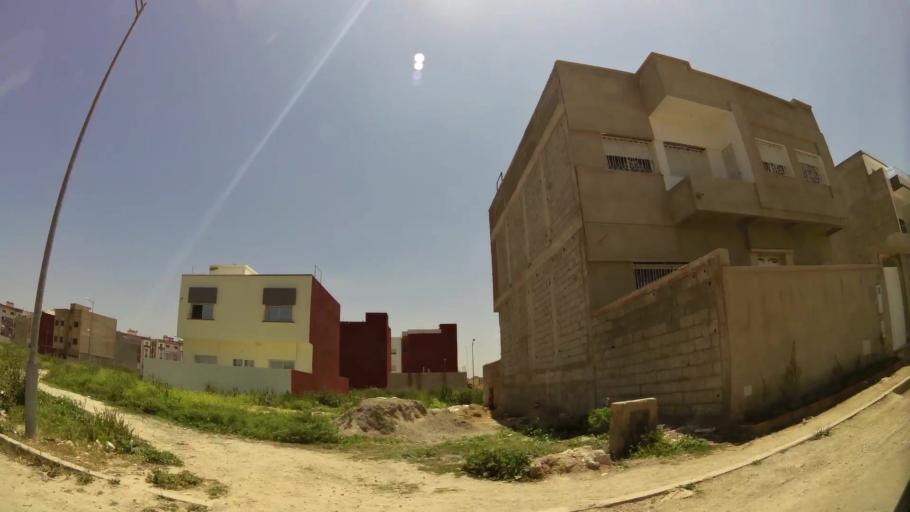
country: MA
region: Fes-Boulemane
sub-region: Fes
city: Fes
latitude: 34.0388
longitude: -5.0463
